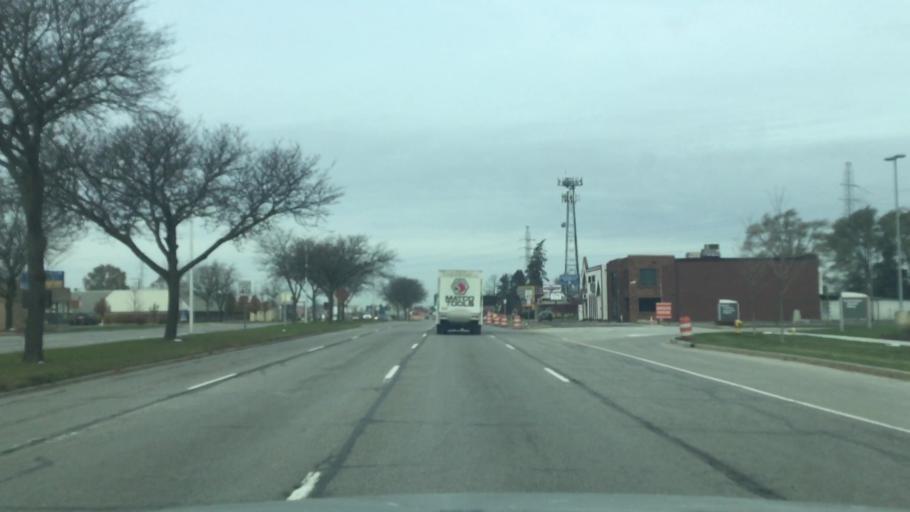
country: US
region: Michigan
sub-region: Oakland County
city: Pontiac
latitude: 42.6167
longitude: -83.2763
